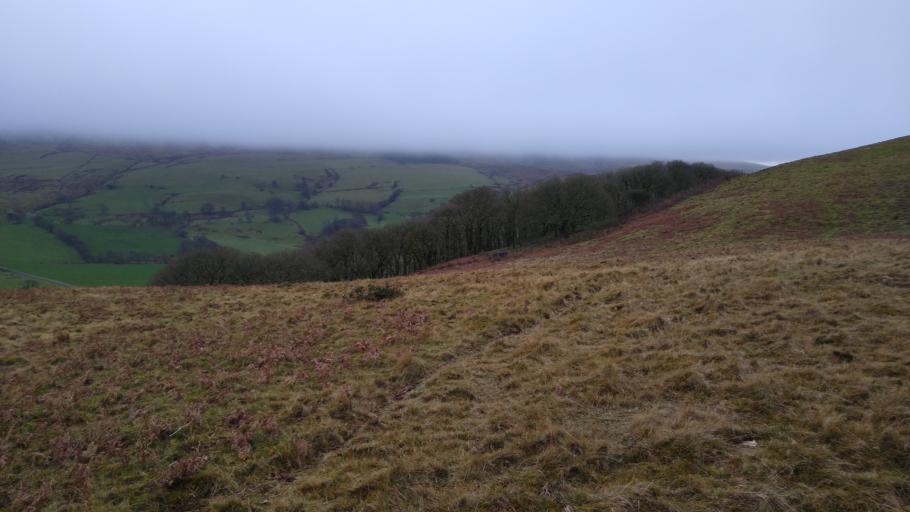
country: GB
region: England
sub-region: Cumbria
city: Cockermouth
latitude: 54.6541
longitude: -3.2416
